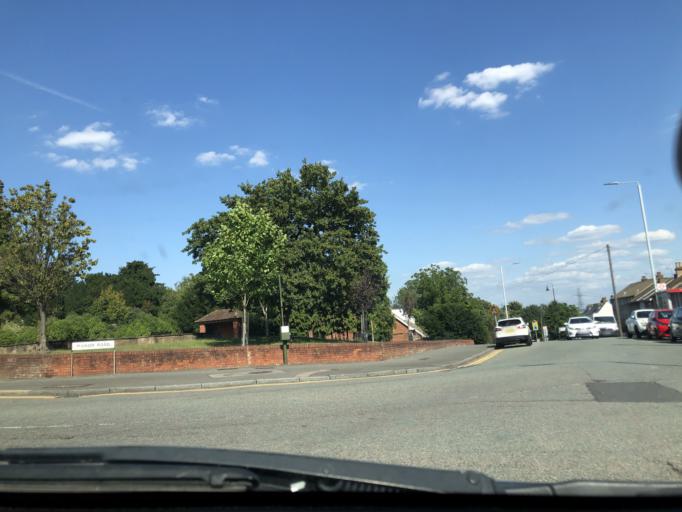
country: GB
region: England
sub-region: Greater London
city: Bexley
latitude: 51.4542
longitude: 0.1733
